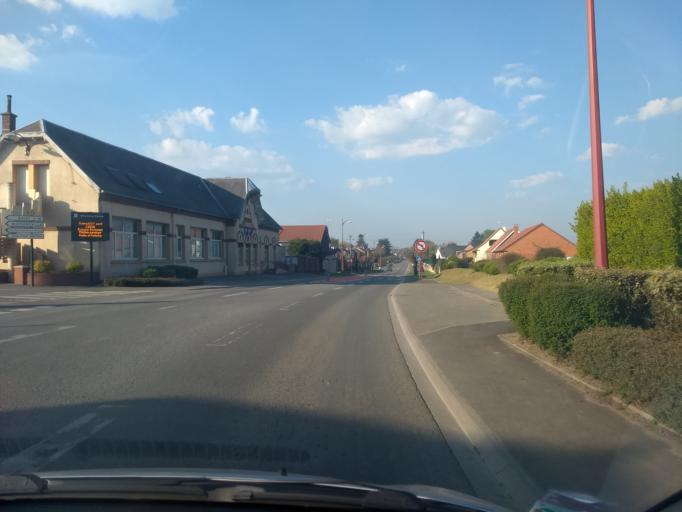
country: FR
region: Nord-Pas-de-Calais
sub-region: Departement du Pas-de-Calais
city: Agny
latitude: 50.2029
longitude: 2.7543
